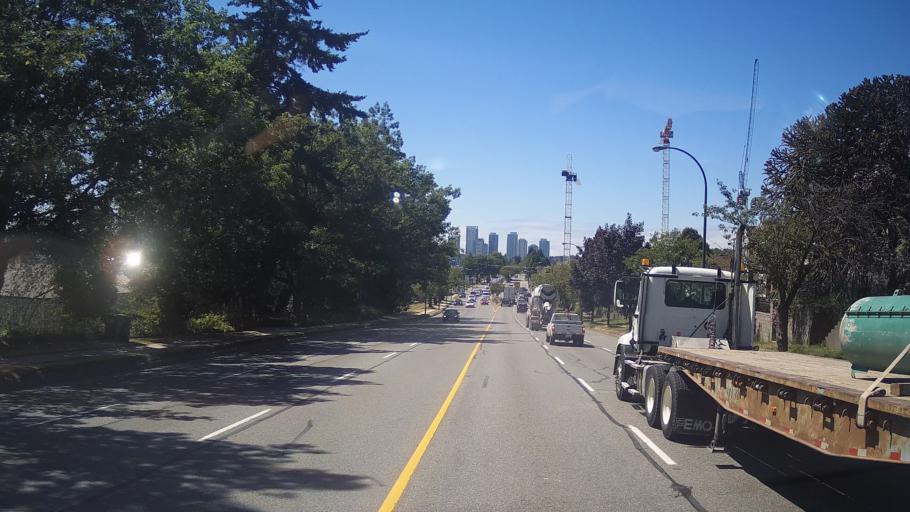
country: CA
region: British Columbia
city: Vancouver
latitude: 49.2111
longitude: -123.0863
